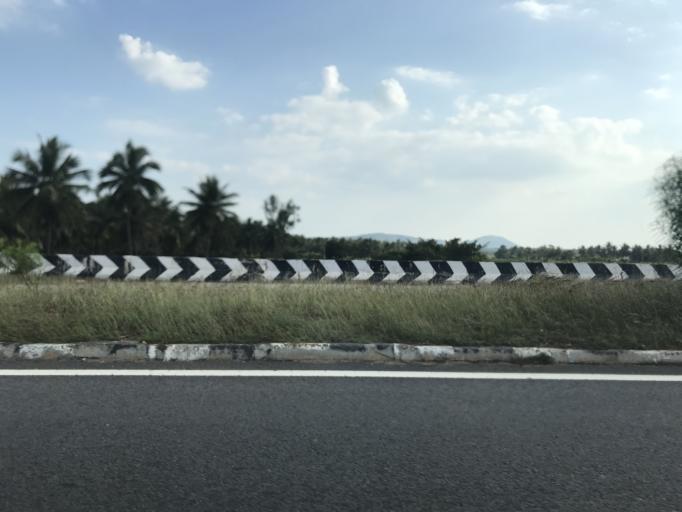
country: IN
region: Karnataka
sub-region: Tumkur
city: Kunigal
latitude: 13.0033
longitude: 76.9720
